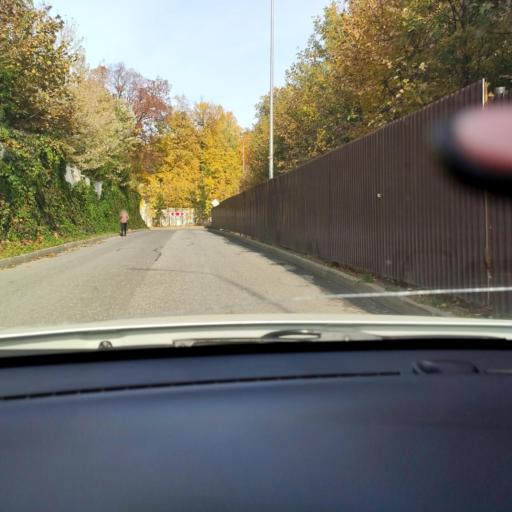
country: RU
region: Tatarstan
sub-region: Gorod Kazan'
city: Kazan
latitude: 55.7418
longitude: 49.1663
